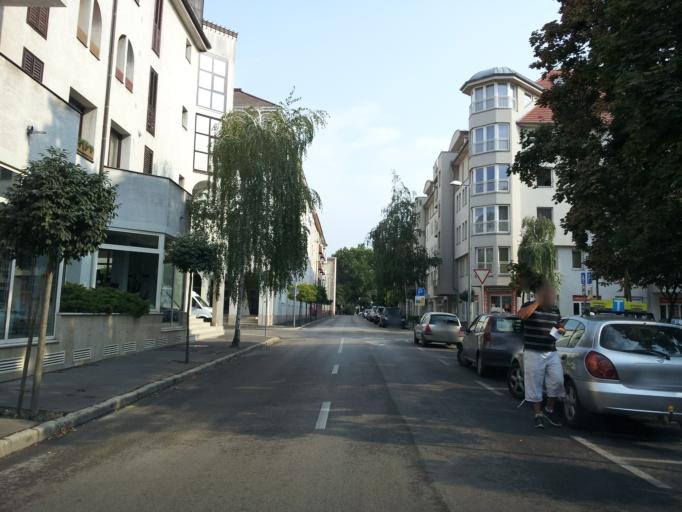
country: HU
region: Gyor-Moson-Sopron
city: Gyor
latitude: 47.6885
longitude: 17.6412
